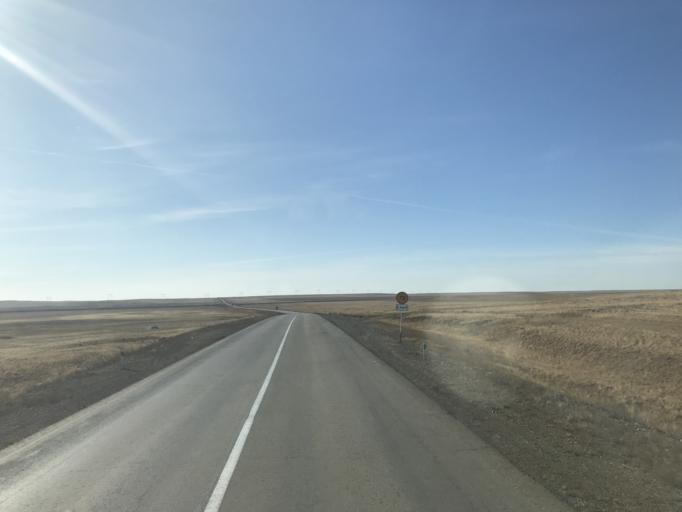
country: RU
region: Orenburg
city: Svetlyy
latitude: 50.5839
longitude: 60.9133
